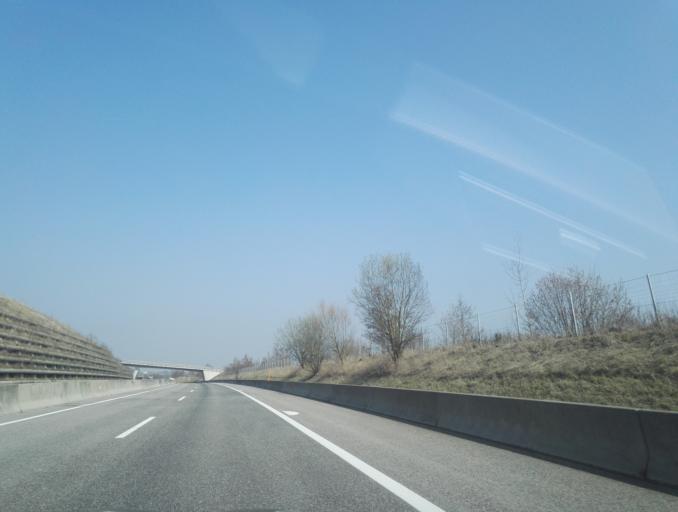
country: AT
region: Upper Austria
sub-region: Wels-Land
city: Steinhaus
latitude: 48.0924
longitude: 14.0217
